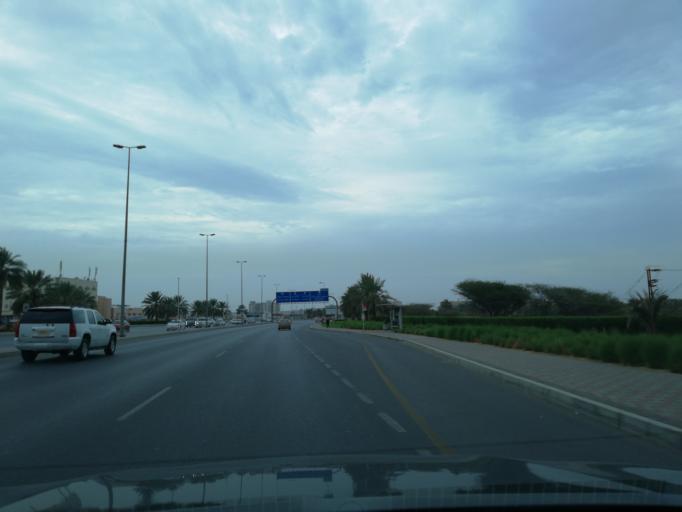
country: OM
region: Muhafazat Masqat
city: Bawshar
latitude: 23.5792
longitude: 58.3820
